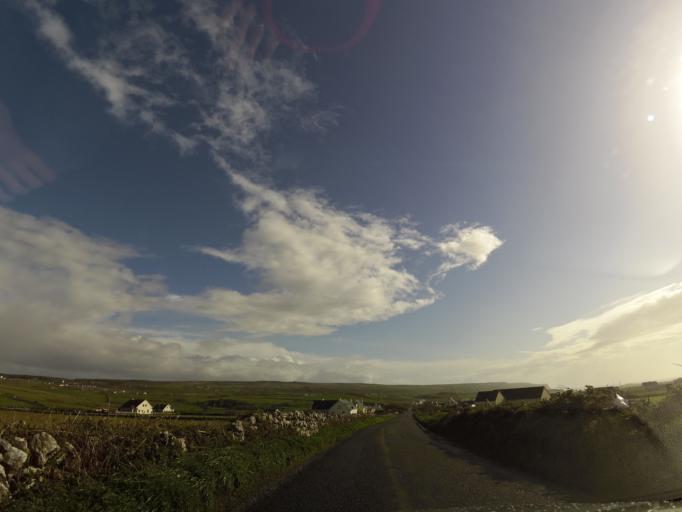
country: IE
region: Connaught
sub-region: County Galway
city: Bearna
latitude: 53.0236
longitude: -9.3680
